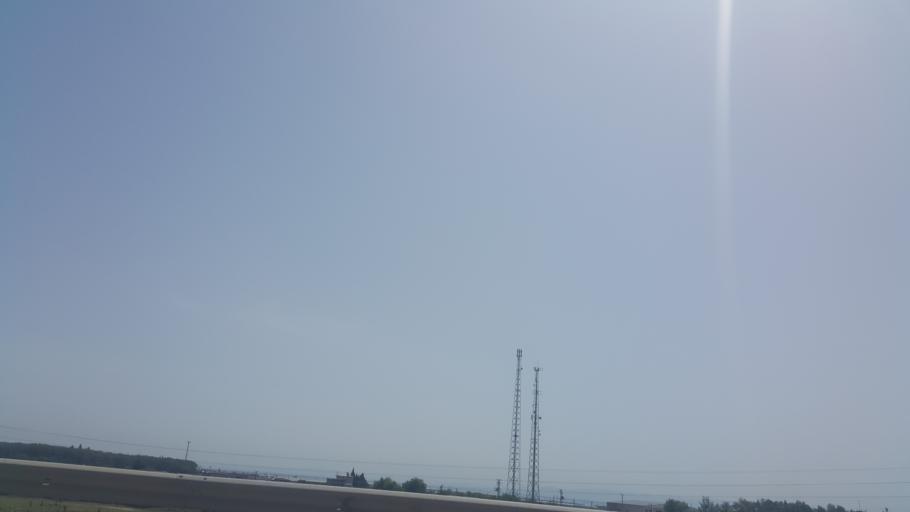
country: TR
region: Hatay
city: Serinyol
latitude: 36.3646
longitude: 36.2232
